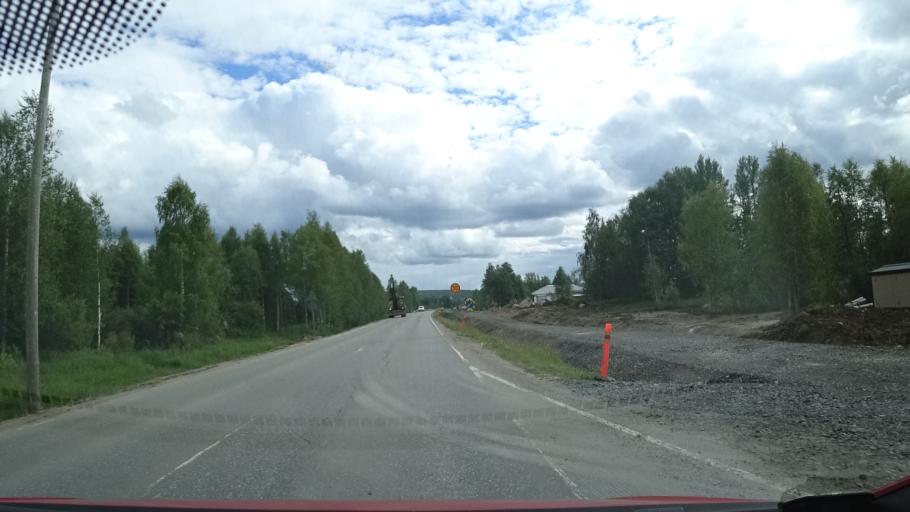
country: FI
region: Lapland
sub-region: Rovaniemi
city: Rovaniemi
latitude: 66.5289
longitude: 25.7394
